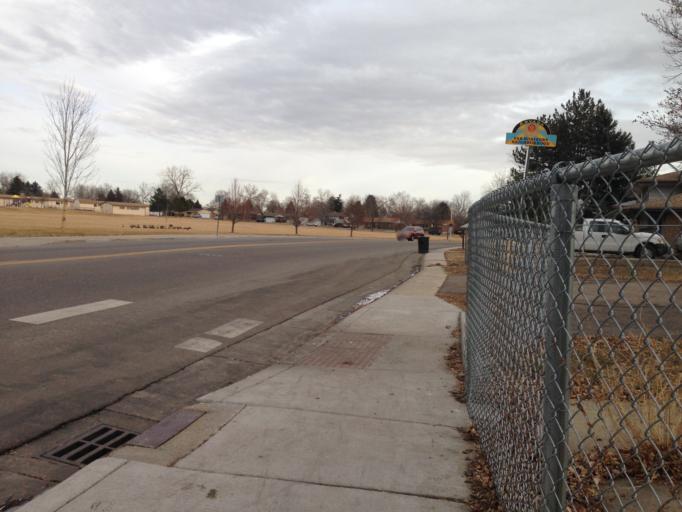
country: US
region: Colorado
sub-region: Adams County
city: Westminster
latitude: 39.8473
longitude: -105.0629
